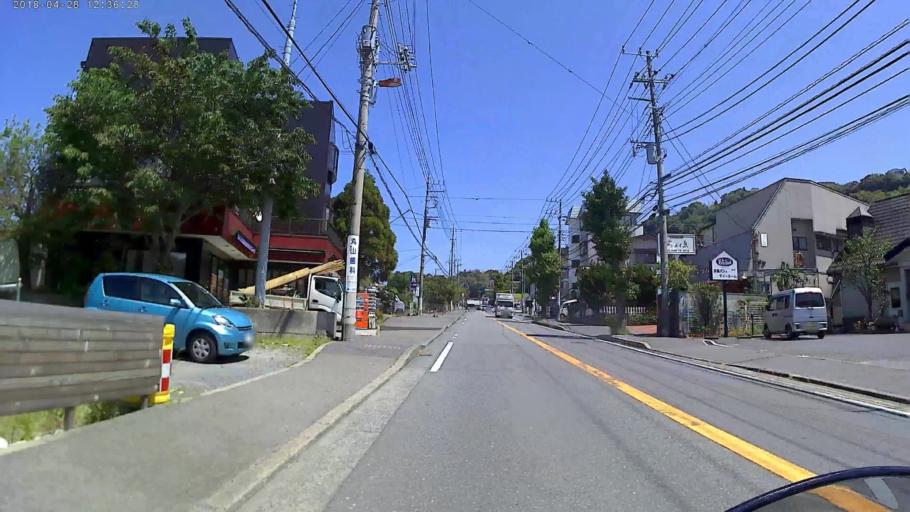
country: JP
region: Kanagawa
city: Hayama
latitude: 35.2654
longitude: 139.5920
